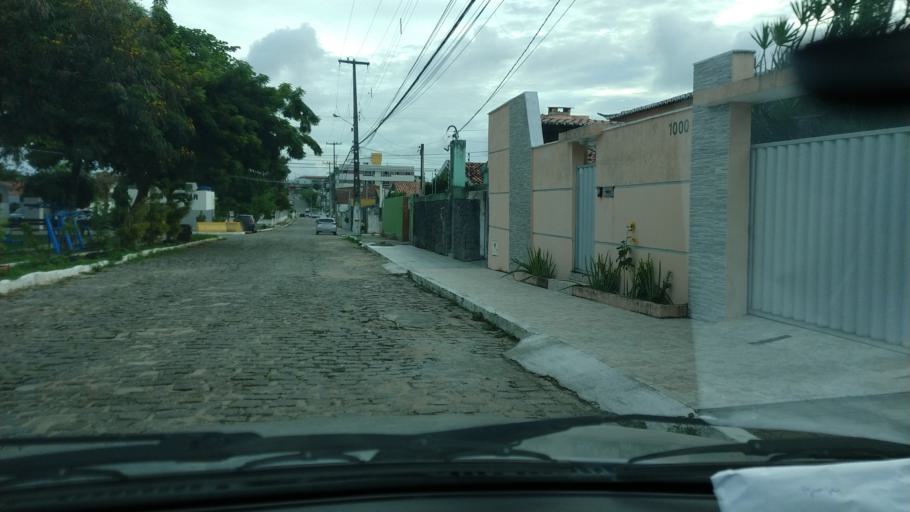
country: BR
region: Rio Grande do Norte
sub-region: Natal
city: Natal
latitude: -5.8208
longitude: -35.1987
